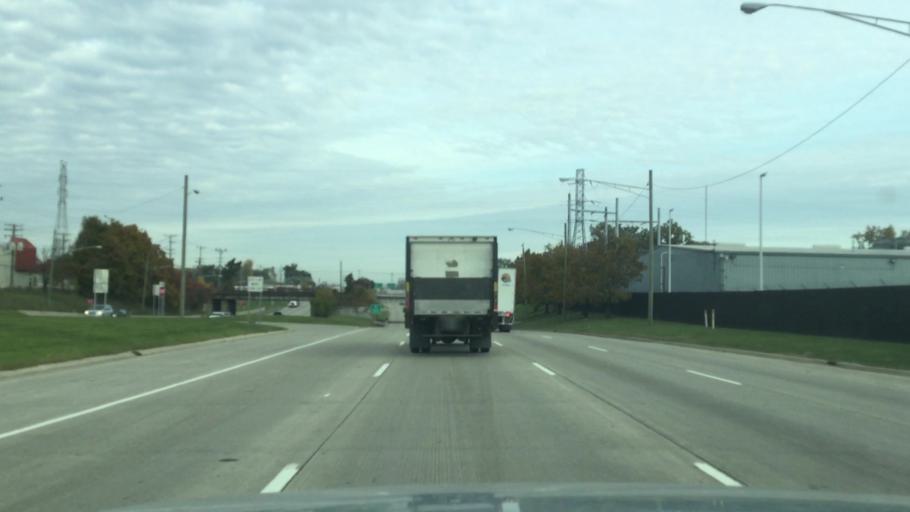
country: US
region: Michigan
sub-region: Wayne County
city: Redford
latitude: 42.3765
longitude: -83.2753
